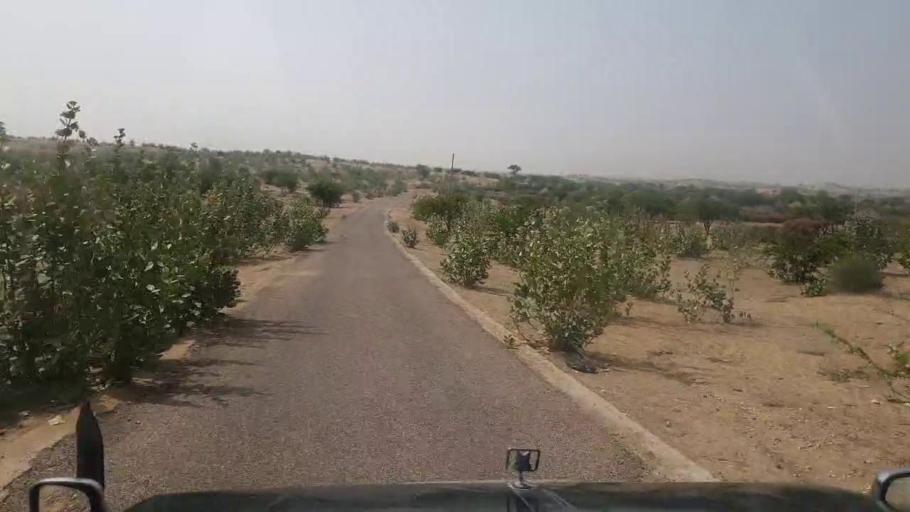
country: PK
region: Sindh
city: Islamkot
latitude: 25.0813
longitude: 70.1547
